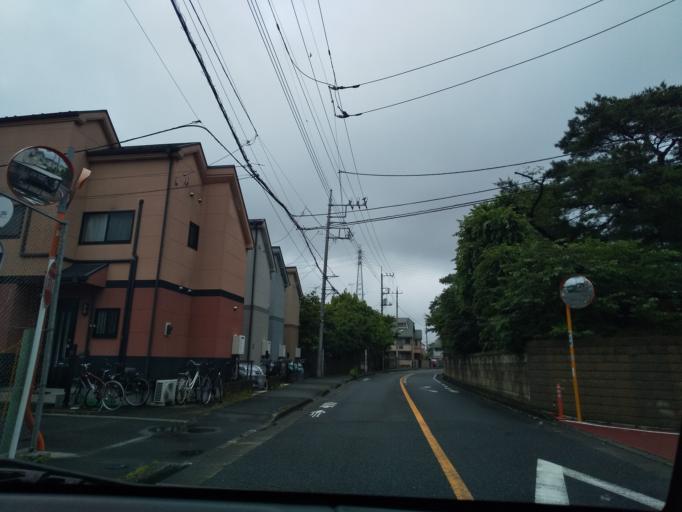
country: JP
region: Tokyo
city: Hino
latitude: 35.6793
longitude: 139.4136
